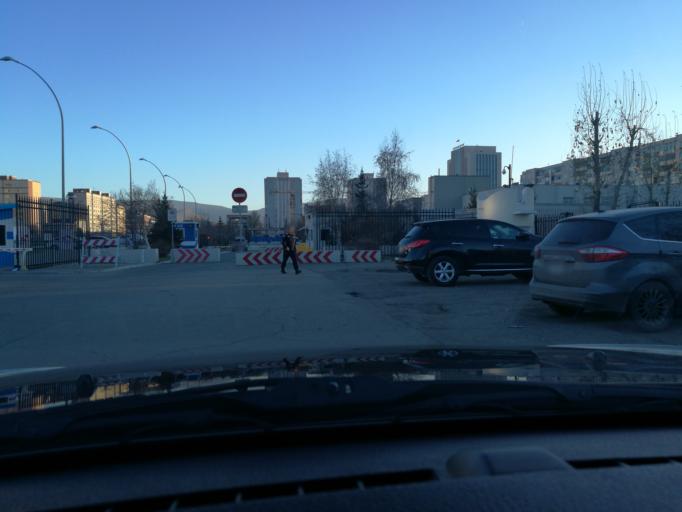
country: MN
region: Ulaanbaatar
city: Ulaanbaatar
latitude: 47.9293
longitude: 106.9306
